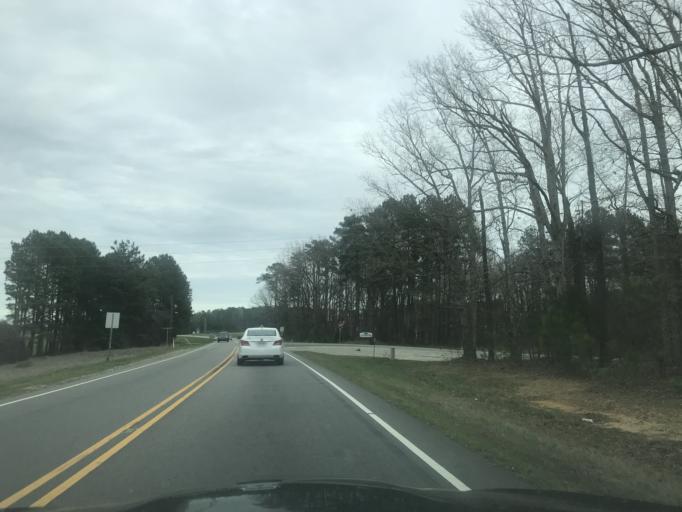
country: US
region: North Carolina
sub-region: Franklin County
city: Louisburg
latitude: 36.0824
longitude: -78.3396
